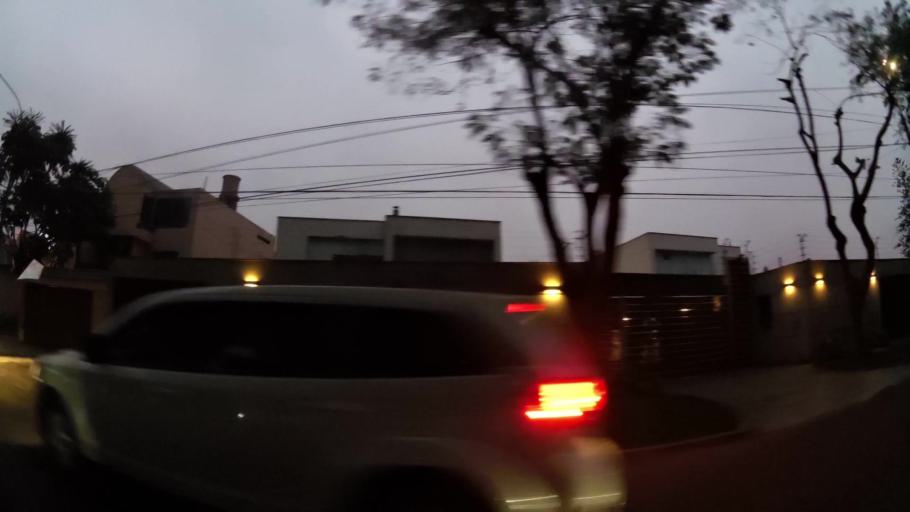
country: PE
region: Lima
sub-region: Lima
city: La Molina
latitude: -12.0870
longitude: -76.9561
